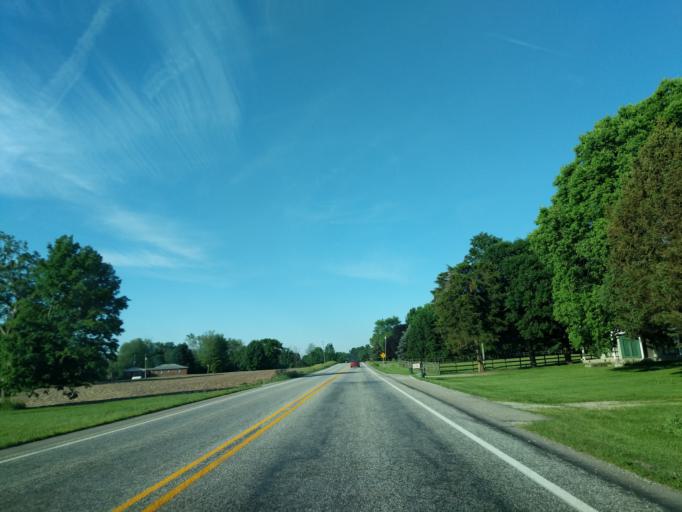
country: US
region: Indiana
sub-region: Madison County
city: Pendleton
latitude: 39.9596
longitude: -85.7601
